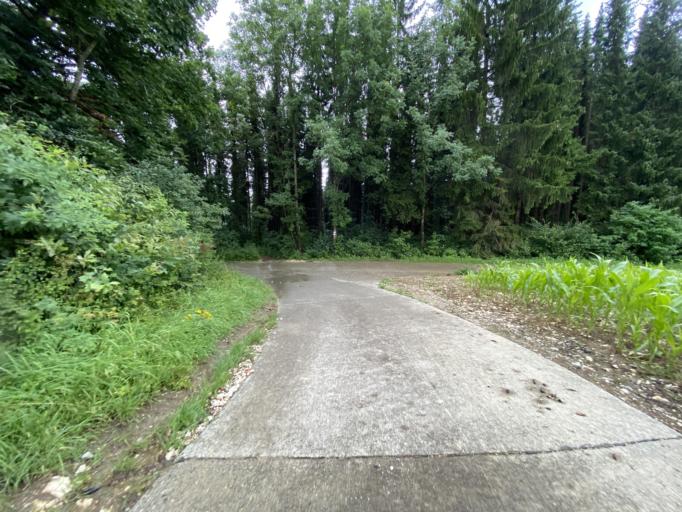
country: DE
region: Baden-Wuerttemberg
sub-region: Tuebingen Region
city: Bingen
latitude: 48.1127
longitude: 9.2531
